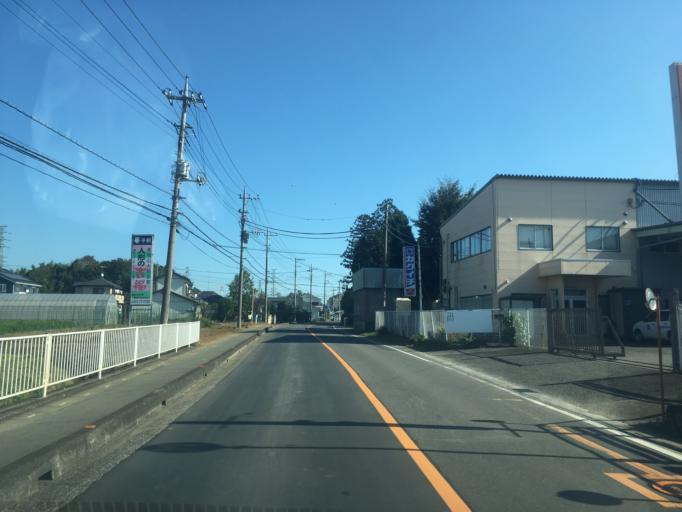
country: JP
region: Saitama
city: Sakado
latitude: 35.9674
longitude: 139.4238
